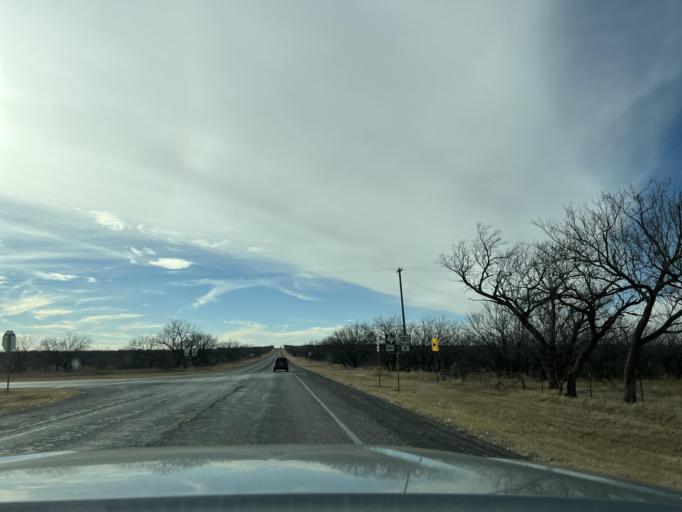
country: US
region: Texas
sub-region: Fisher County
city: Roby
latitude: 32.7596
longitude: -100.3157
